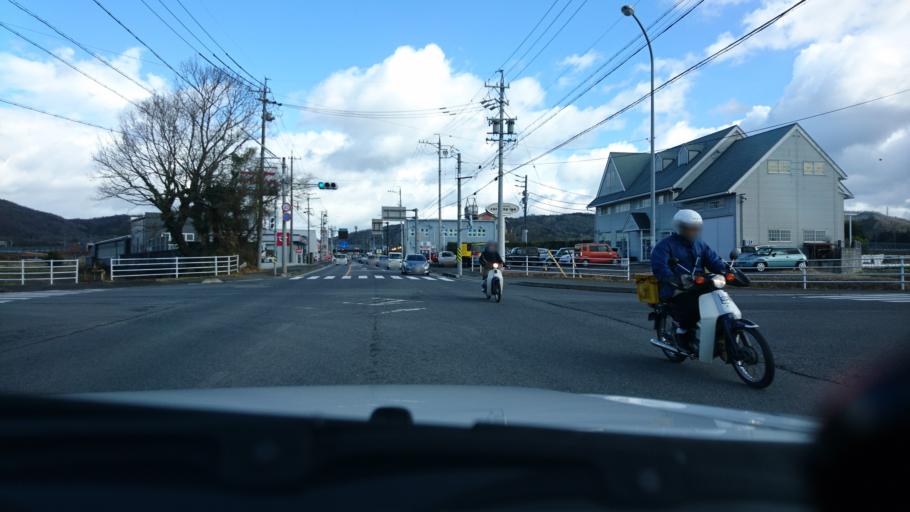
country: JP
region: Mie
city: Ueno-ebisumachi
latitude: 34.7713
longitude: 136.1534
